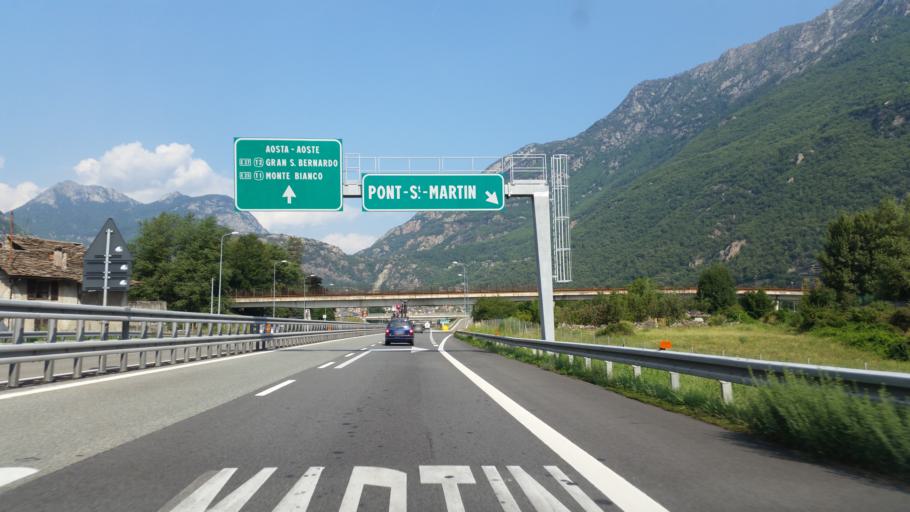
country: IT
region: Aosta Valley
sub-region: Valle d'Aosta
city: Pont-Saint-Martin
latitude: 45.5922
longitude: 7.7894
